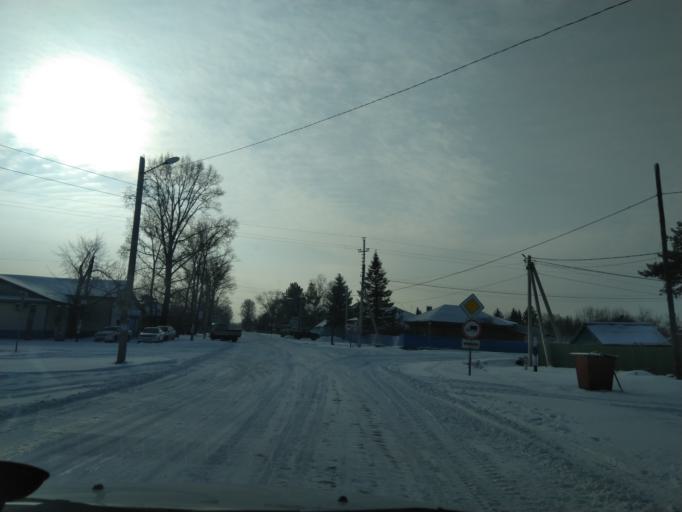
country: RU
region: Amur
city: Poyarkovo
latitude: 49.6289
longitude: 128.6498
